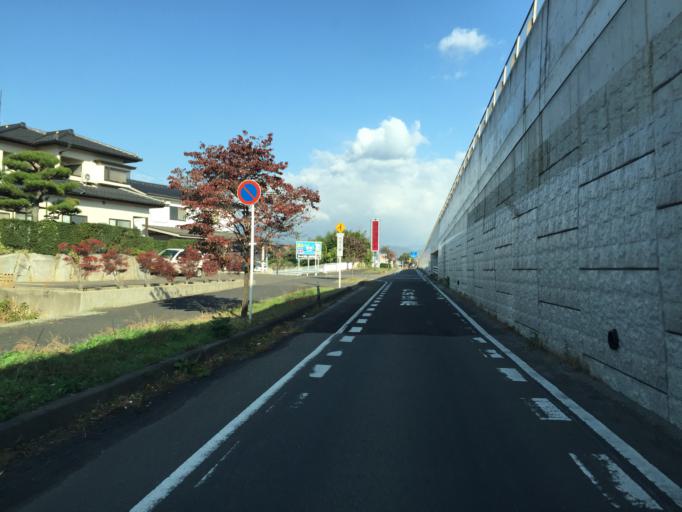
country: JP
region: Fukushima
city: Fukushima-shi
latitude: 37.7413
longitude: 140.4391
